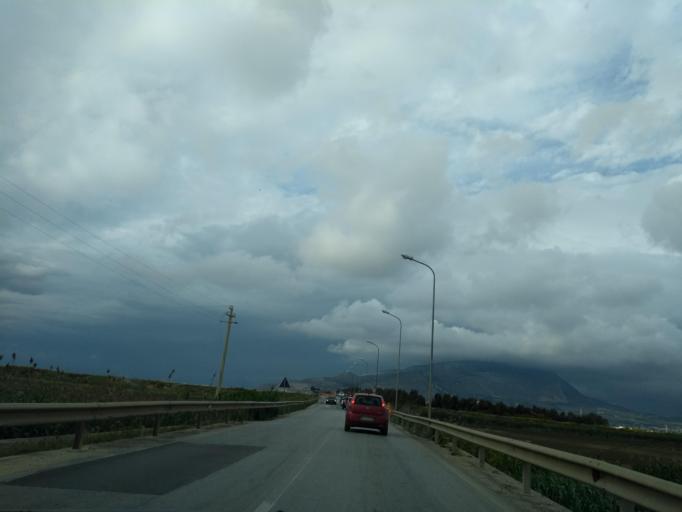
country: IT
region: Sicily
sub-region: Trapani
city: Paceco
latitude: 37.9849
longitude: 12.5324
